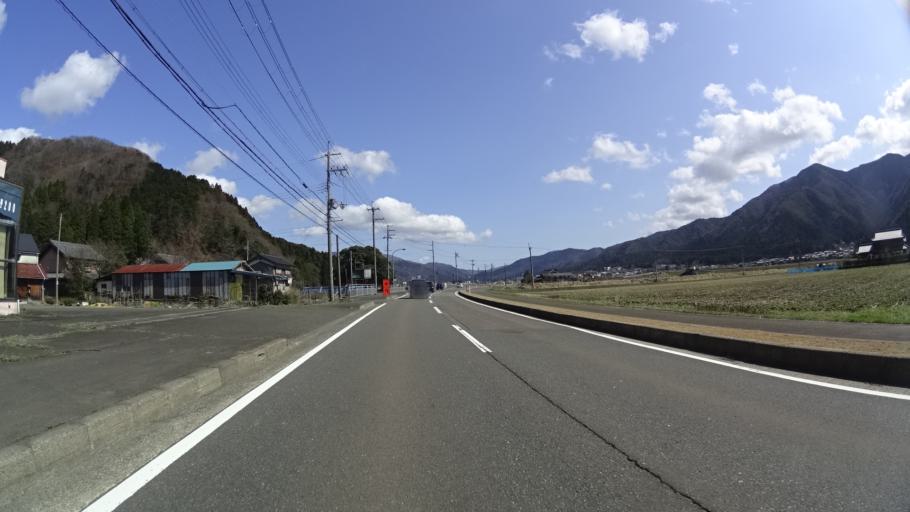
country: JP
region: Fukui
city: Obama
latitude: 35.4720
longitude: 135.8410
